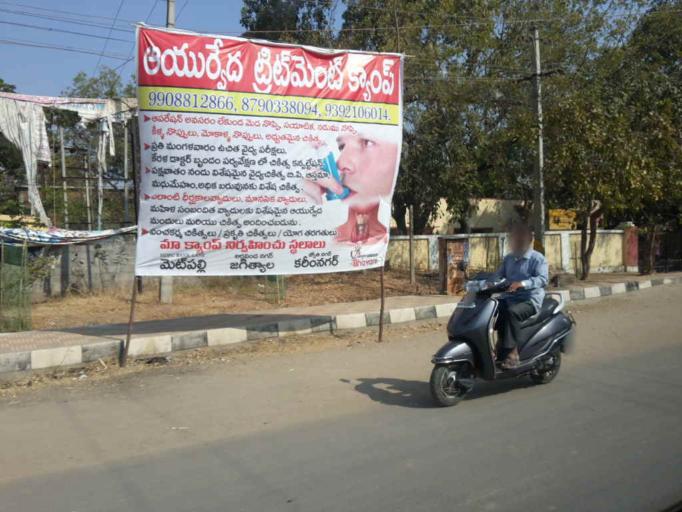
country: IN
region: Telangana
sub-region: Karimnagar
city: Koratla
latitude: 18.8489
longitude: 78.6185
